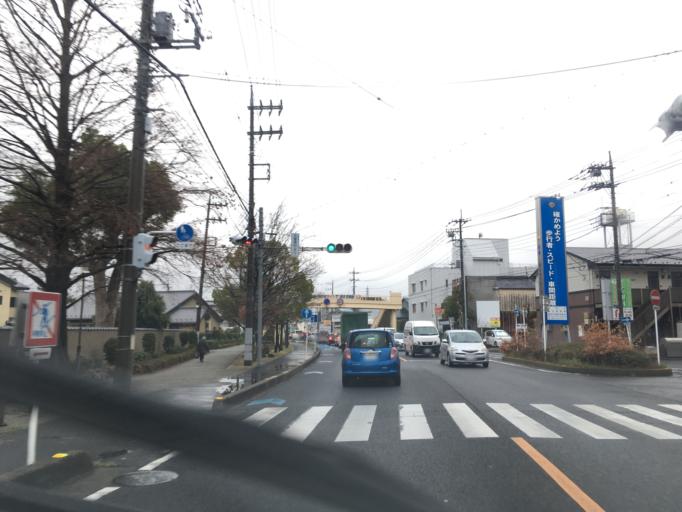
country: JP
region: Saitama
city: Koshigaya
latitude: 35.8870
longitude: 139.7913
